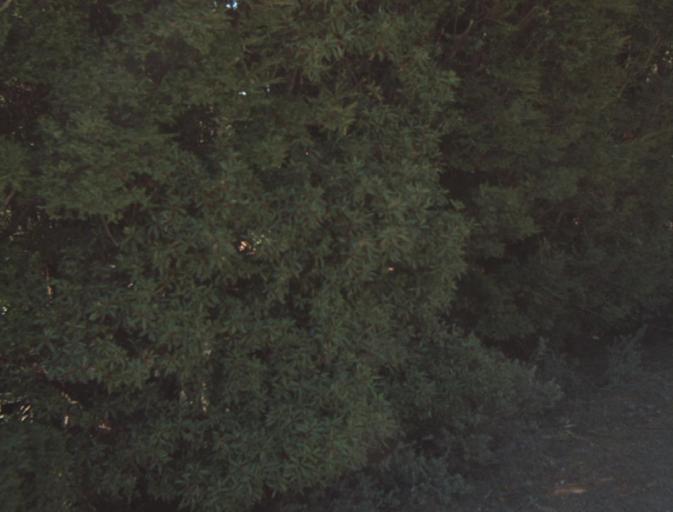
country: AU
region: Tasmania
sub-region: Dorset
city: Scottsdale
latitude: -41.3644
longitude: 147.4315
